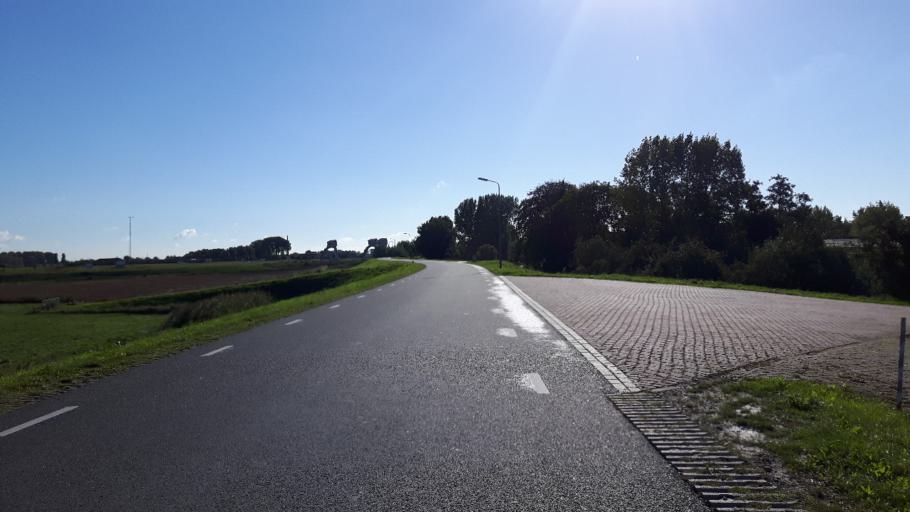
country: NL
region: Utrecht
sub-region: Gemeente Vianen
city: Vianen
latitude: 51.9943
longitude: 5.1232
